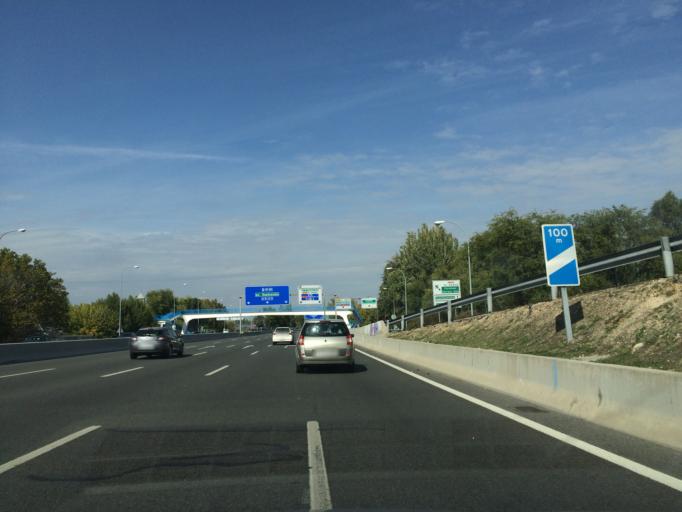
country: ES
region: Madrid
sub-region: Provincia de Madrid
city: Tetuan de las Victorias
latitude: 40.4695
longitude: -3.7501
